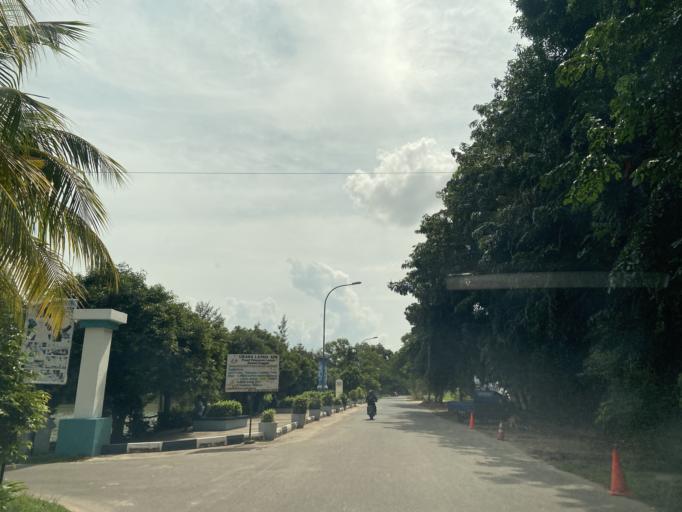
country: SG
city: Singapore
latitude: 1.1258
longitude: 104.0507
